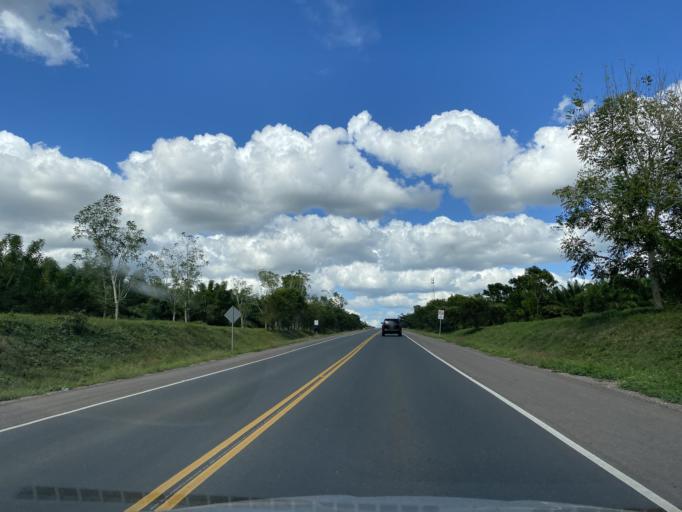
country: DO
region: Monte Plata
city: Monte Plata
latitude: 18.7240
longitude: -69.7606
